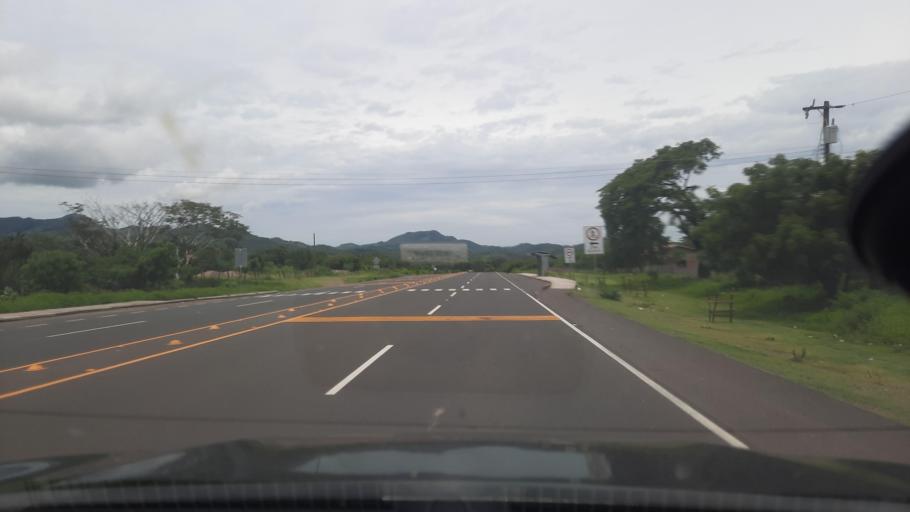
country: HN
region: Valle
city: Aramecina
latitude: 13.7241
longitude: -87.7100
